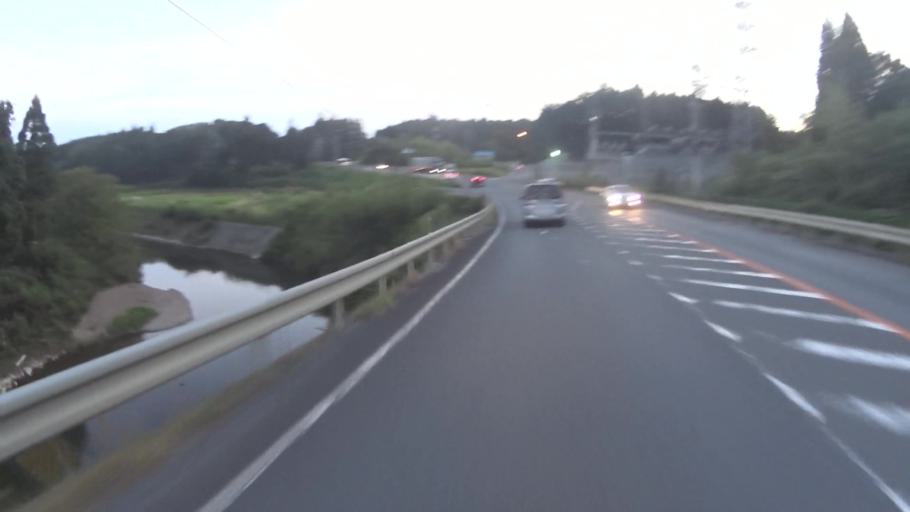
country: JP
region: Kyoto
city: Ayabe
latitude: 35.2062
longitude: 135.4342
